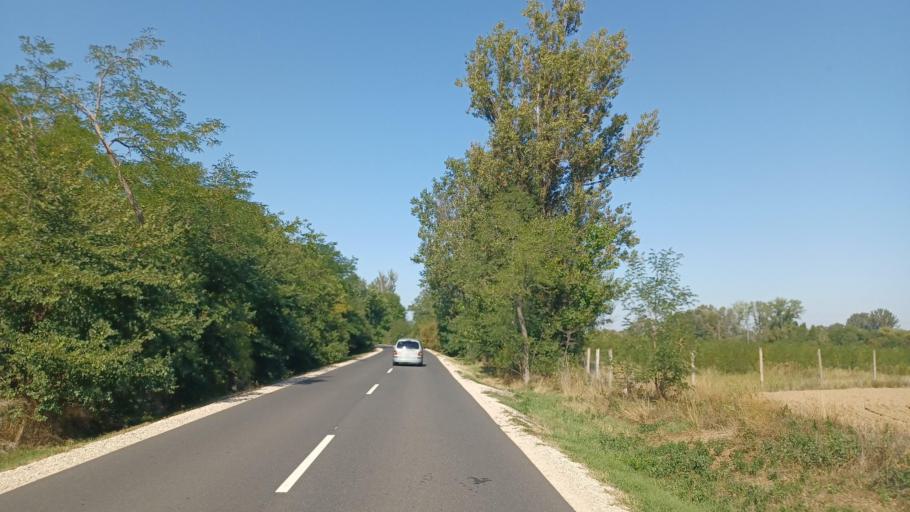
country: HU
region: Fejer
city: Alap
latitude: 46.7453
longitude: 18.6925
